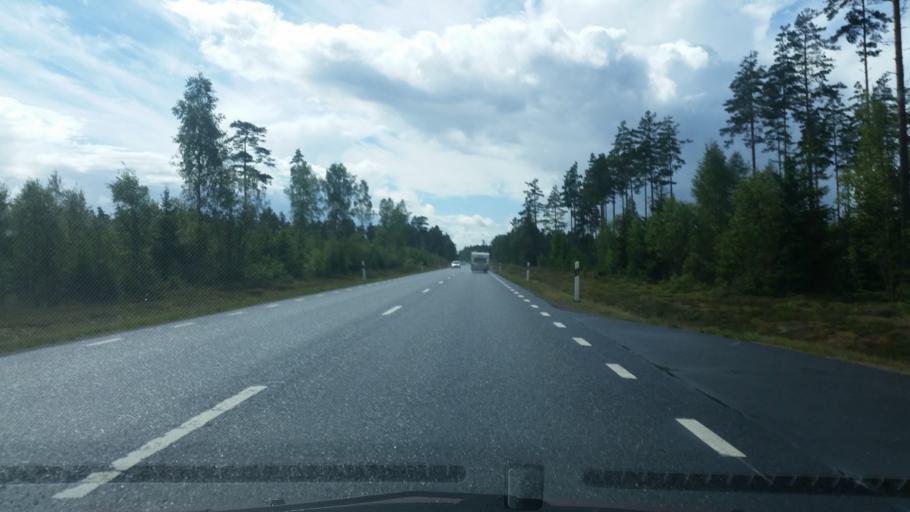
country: SE
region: Joenkoeping
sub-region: Gislaveds Kommun
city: Gislaved
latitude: 57.4004
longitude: 13.5957
